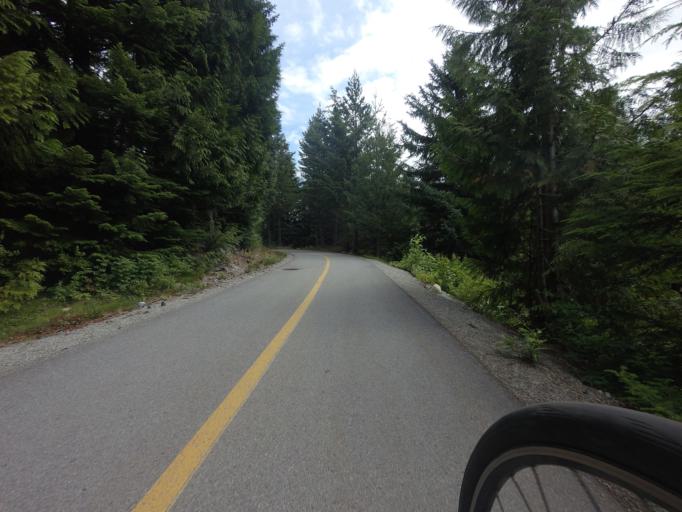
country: CA
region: British Columbia
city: Whistler
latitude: 50.1123
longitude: -122.9671
